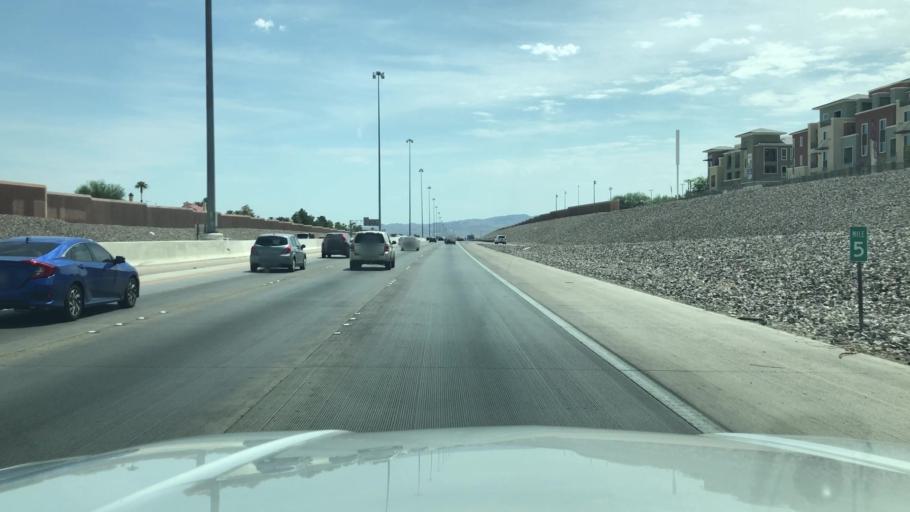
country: US
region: Nevada
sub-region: Clark County
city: Whitney
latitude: 36.0248
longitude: -115.0824
